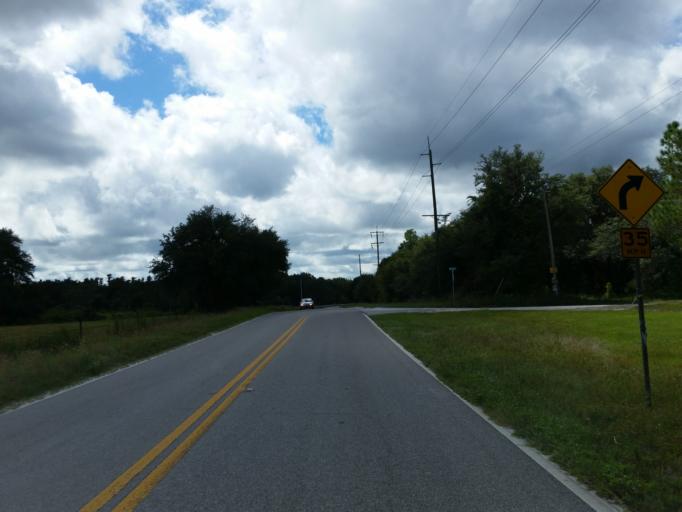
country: US
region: Florida
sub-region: Pasco County
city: Zephyrhills West
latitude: 28.1779
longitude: -82.2536
